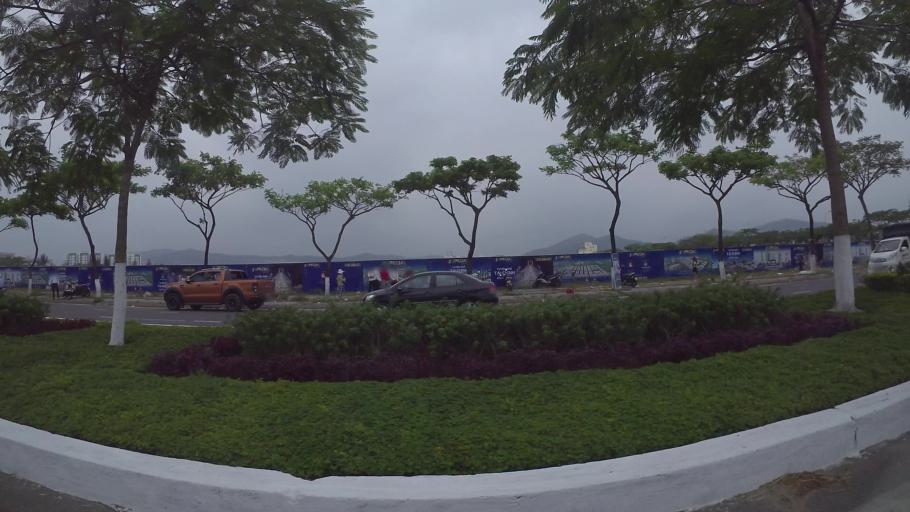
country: VN
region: Da Nang
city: Lien Chieu
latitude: 16.0732
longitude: 108.1617
